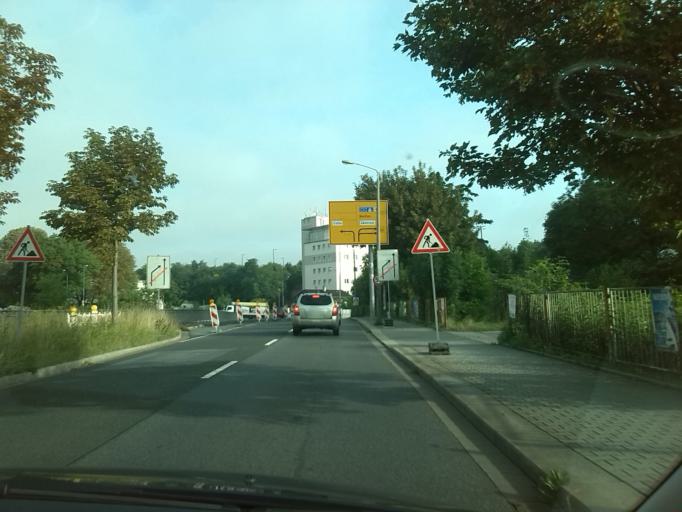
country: DE
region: Saxony
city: Dresden
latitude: 51.0569
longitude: 13.6899
